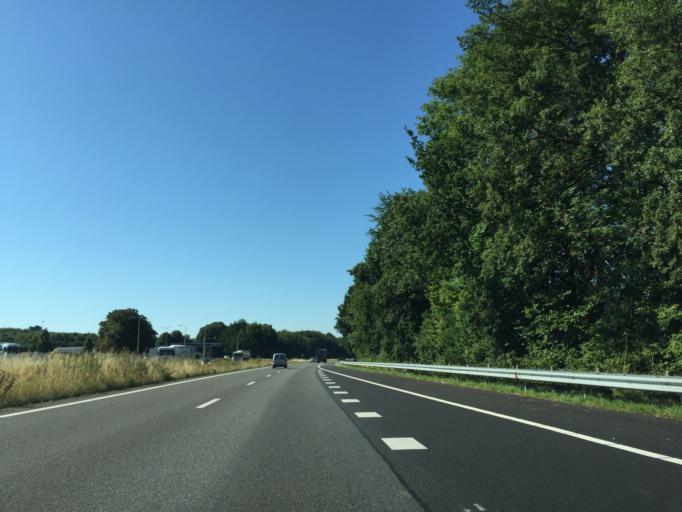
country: NL
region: Limburg
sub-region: Eijsden-Margraten
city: Eijsden
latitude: 50.7794
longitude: 5.7291
